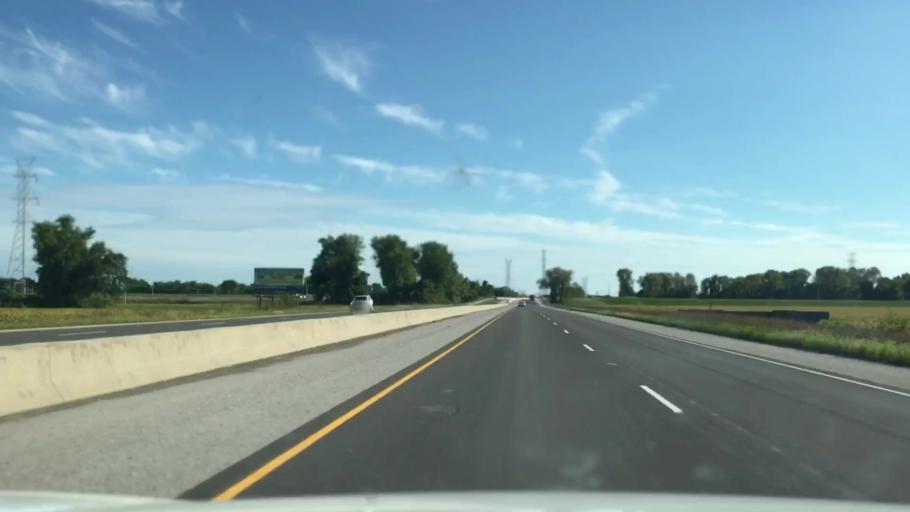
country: US
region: Illinois
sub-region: Madison County
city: Hartford
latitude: 38.8108
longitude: -90.0988
